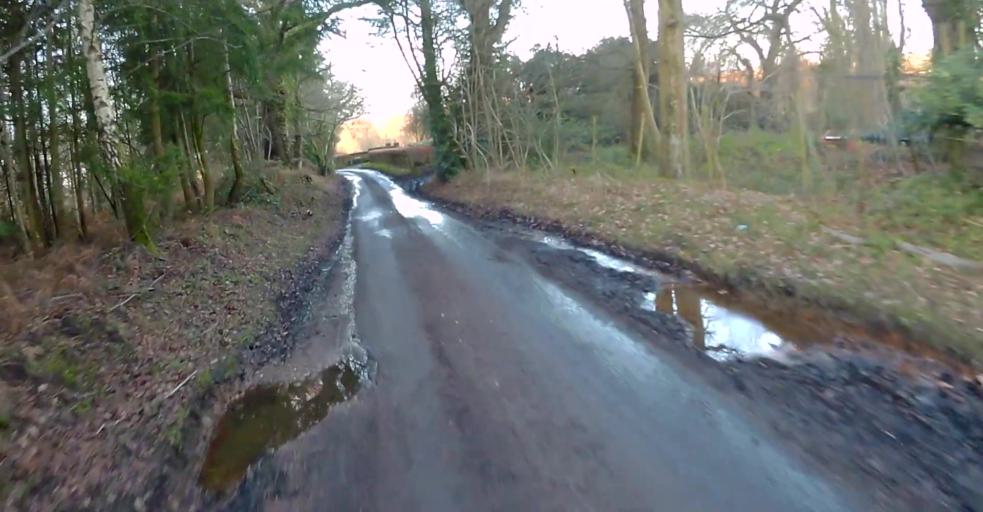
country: GB
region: England
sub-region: Wokingham
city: Swallowfield
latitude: 51.3328
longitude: -0.9888
